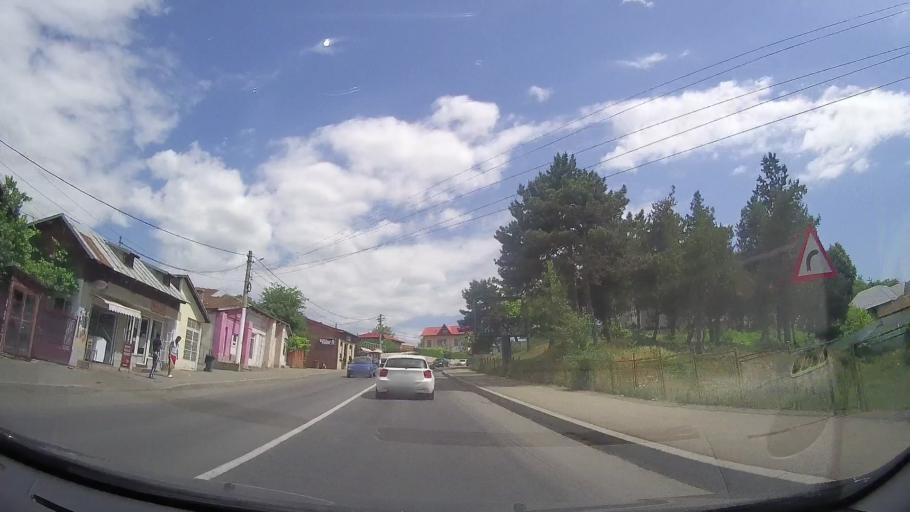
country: RO
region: Prahova
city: Valenii de Munte
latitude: 45.1882
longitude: 26.0417
